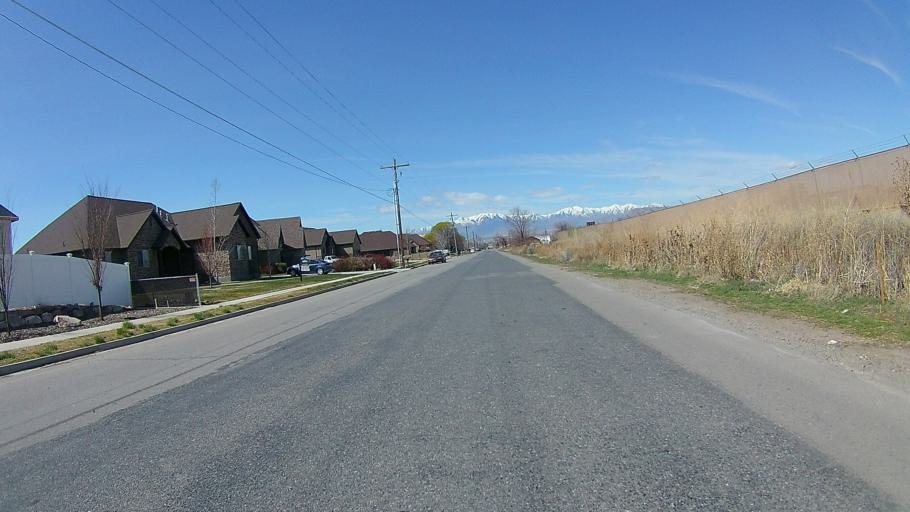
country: US
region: Utah
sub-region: Utah County
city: American Fork
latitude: 40.3727
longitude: -111.8138
